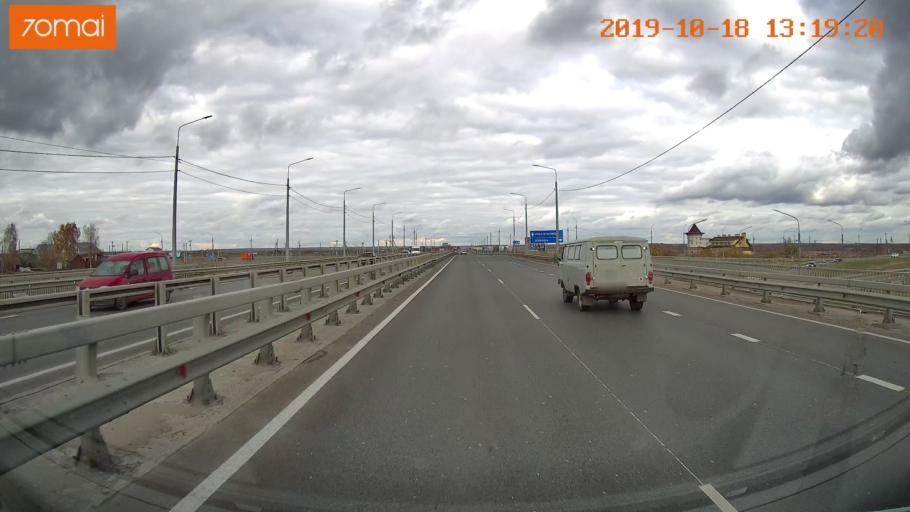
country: RU
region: Rjazan
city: Polyany
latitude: 54.6660
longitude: 39.8243
